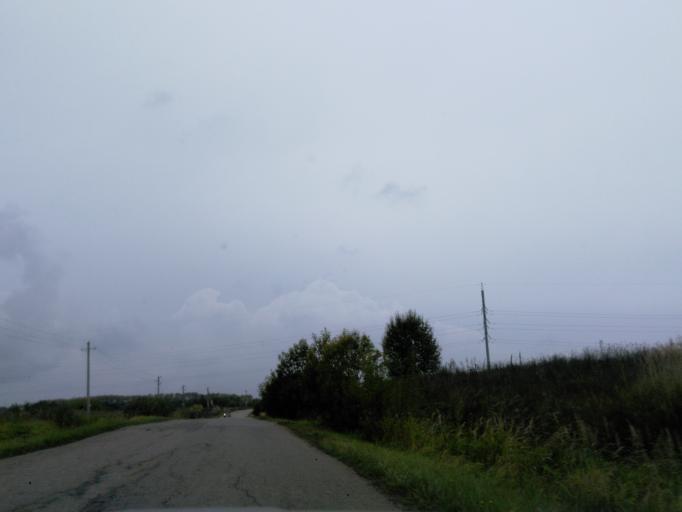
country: RU
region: Moskovskaya
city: Mendeleyevo
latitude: 56.1124
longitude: 37.2258
